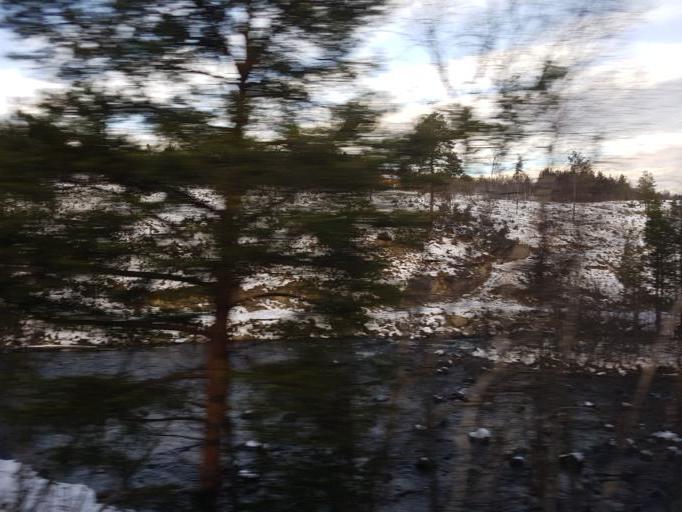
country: NO
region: Sor-Trondelag
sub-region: Rennebu
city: Berkak
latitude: 62.7019
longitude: 9.9473
